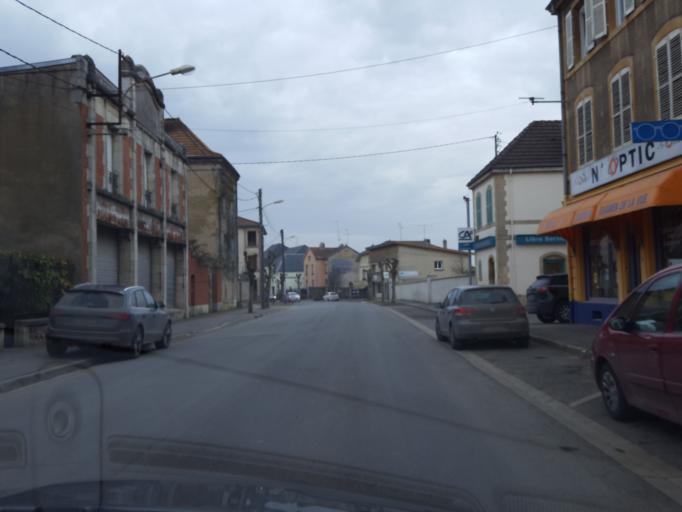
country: FR
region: Lorraine
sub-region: Departement de la Meuse
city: Etain
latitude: 49.2115
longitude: 5.6357
